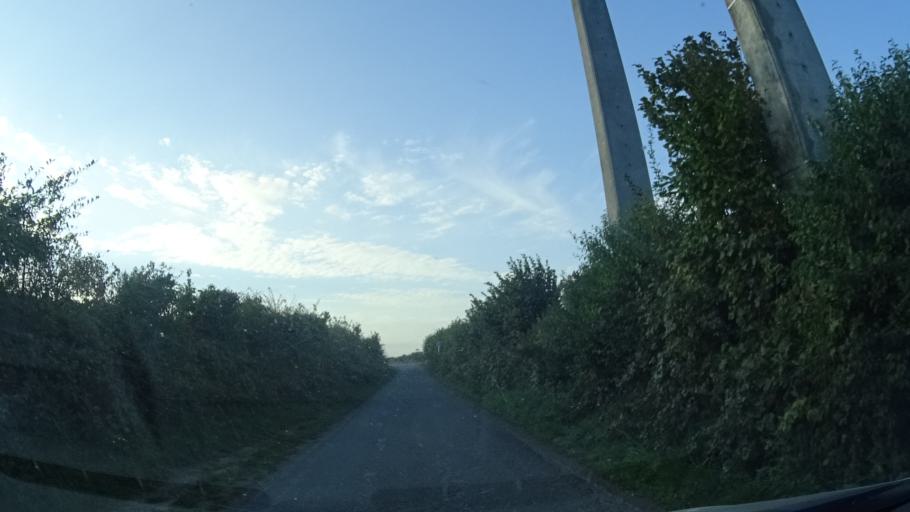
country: BE
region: Wallonia
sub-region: Province du Hainaut
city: Beaumont
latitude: 50.2397
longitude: 4.2696
